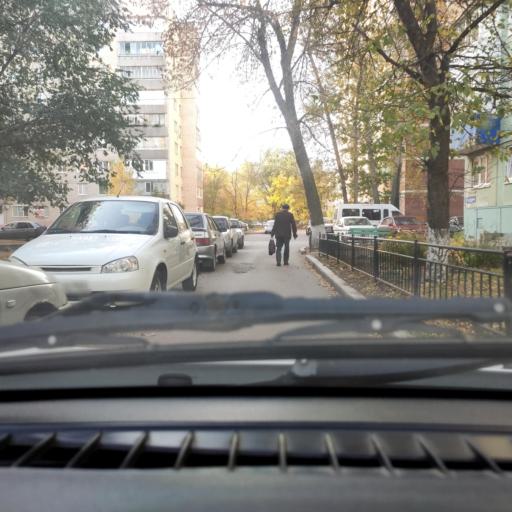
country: RU
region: Samara
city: Tol'yatti
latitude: 53.5041
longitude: 49.4183
